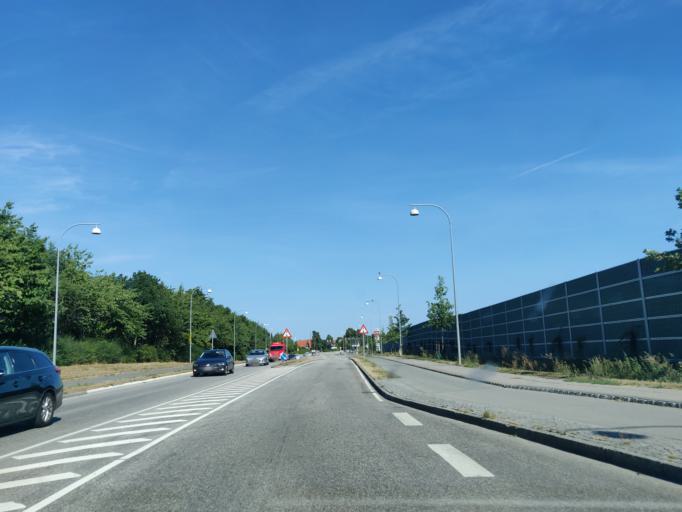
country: DK
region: Zealand
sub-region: Roskilde Kommune
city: Roskilde
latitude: 55.6356
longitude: 12.0485
